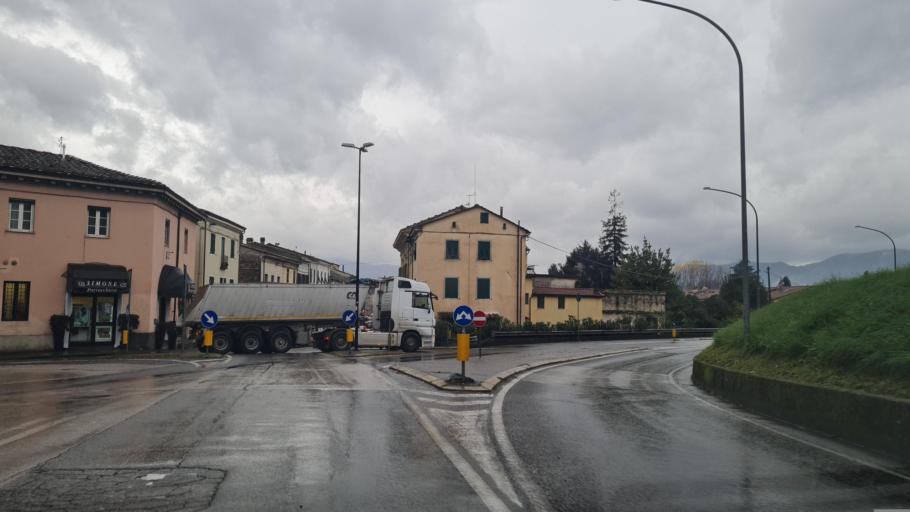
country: IT
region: Tuscany
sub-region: Provincia di Lucca
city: Lucca
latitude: 43.8554
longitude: 10.5079
